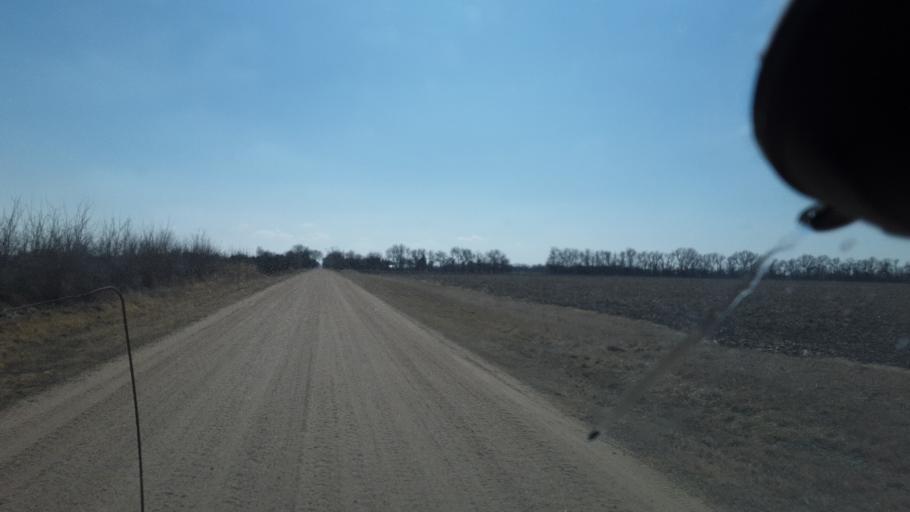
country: US
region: Kansas
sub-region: Reno County
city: Haven
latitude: 37.9227
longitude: -97.8485
